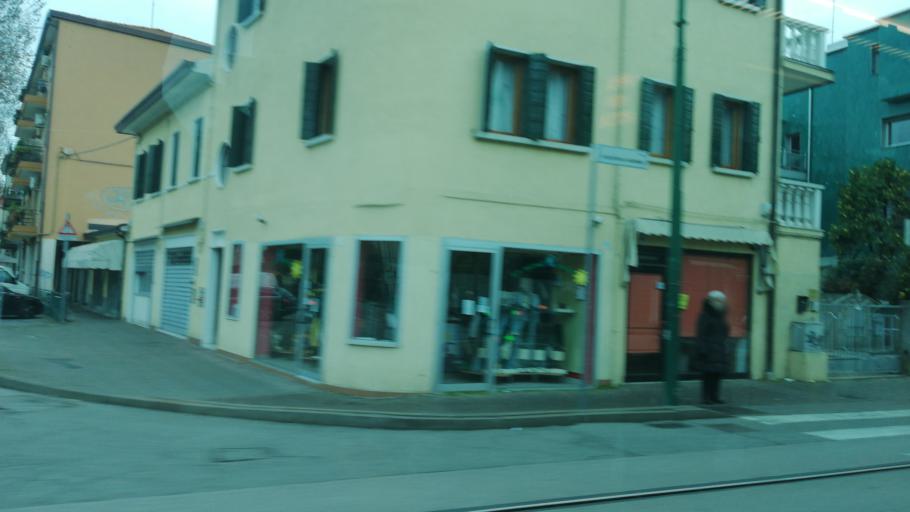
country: IT
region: Veneto
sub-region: Provincia di Venezia
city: Mestre
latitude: 45.4957
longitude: 12.2482
